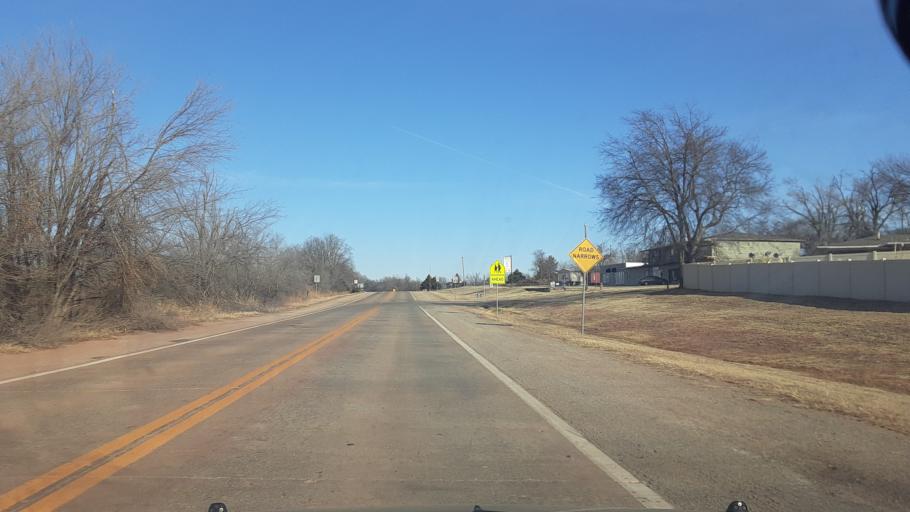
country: US
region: Oklahoma
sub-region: Logan County
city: Guthrie
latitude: 35.8903
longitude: -97.4240
